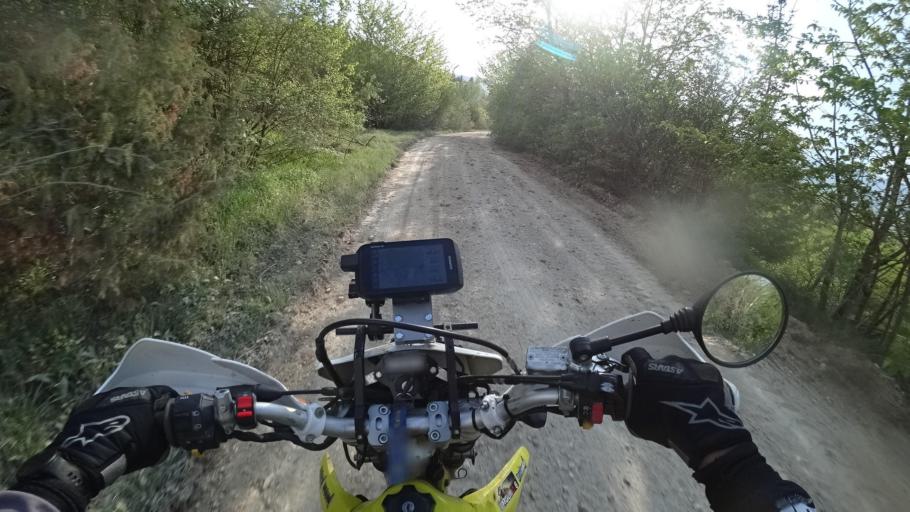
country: BA
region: Federation of Bosnia and Herzegovina
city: Glamoc
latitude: 44.0707
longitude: 16.7816
